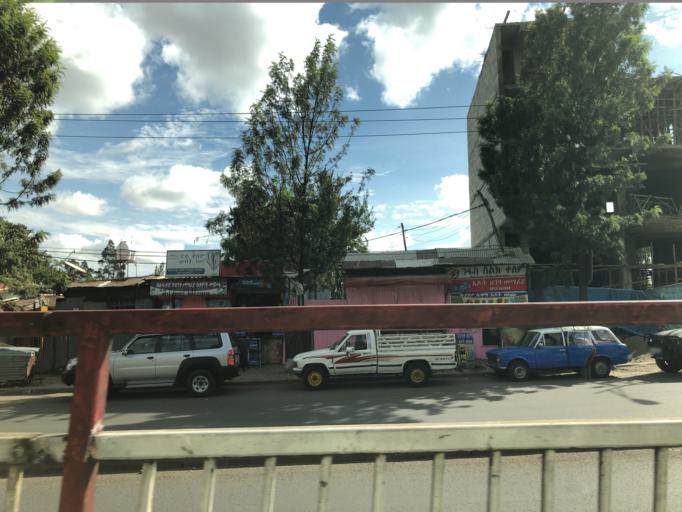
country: ET
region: Adis Abeba
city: Addis Ababa
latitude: 9.0235
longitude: 38.7772
